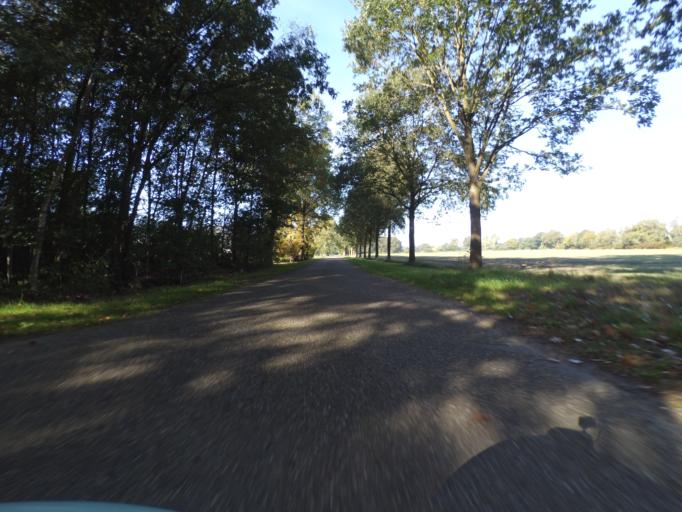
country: NL
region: Gelderland
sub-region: Berkelland
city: Borculo
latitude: 52.0854
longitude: 6.4969
